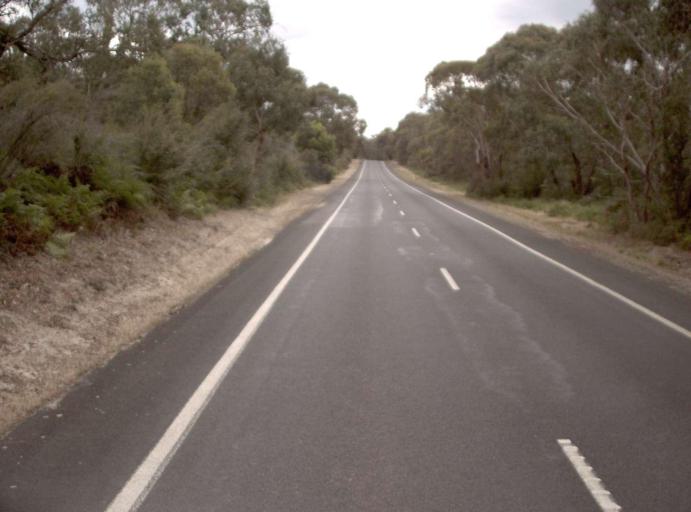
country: AU
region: Victoria
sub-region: Wellington
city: Sale
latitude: -38.2645
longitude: 147.0359
